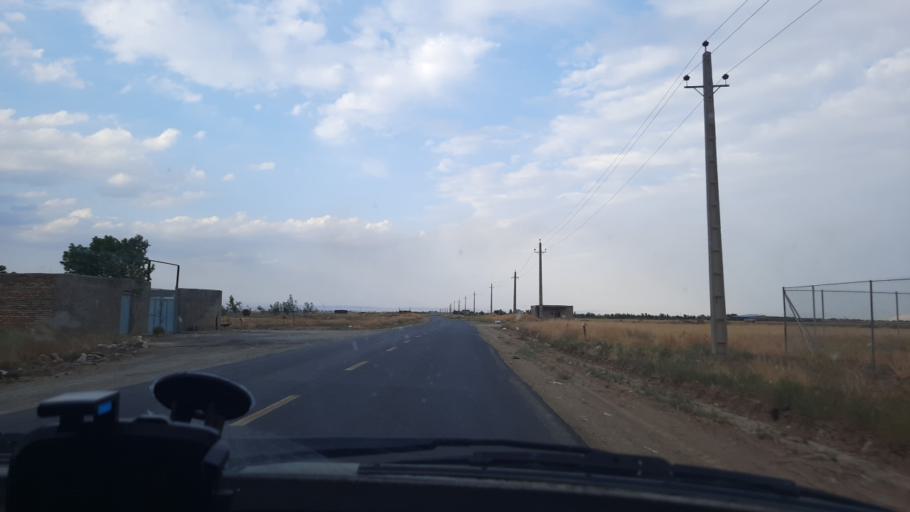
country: IR
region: Markazi
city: Arak
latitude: 34.1304
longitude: 49.7391
